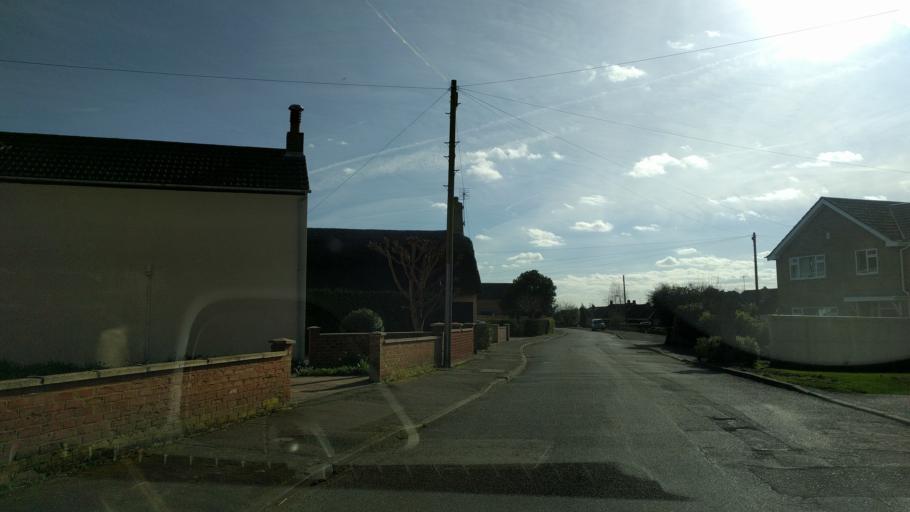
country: GB
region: England
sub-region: Cambridgeshire
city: Chatteris
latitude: 52.4496
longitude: 0.0410
